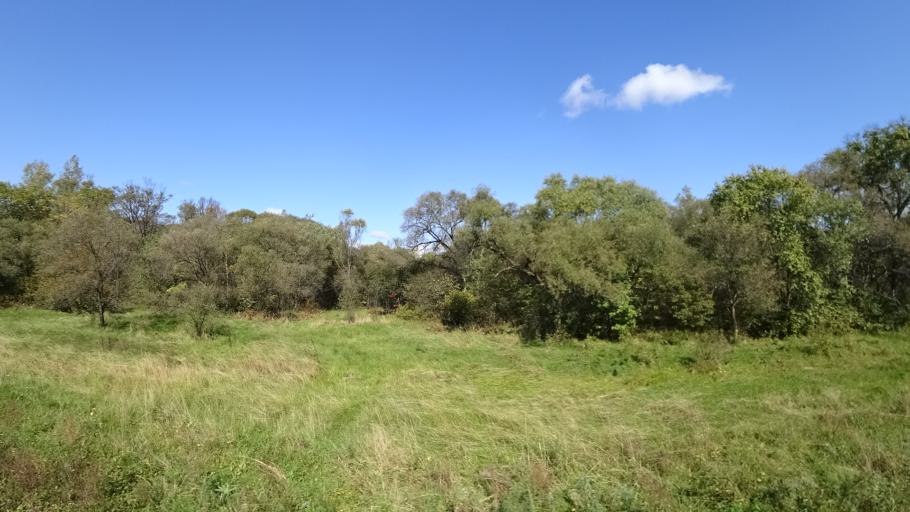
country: RU
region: Amur
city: Arkhara
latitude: 49.4052
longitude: 130.1276
